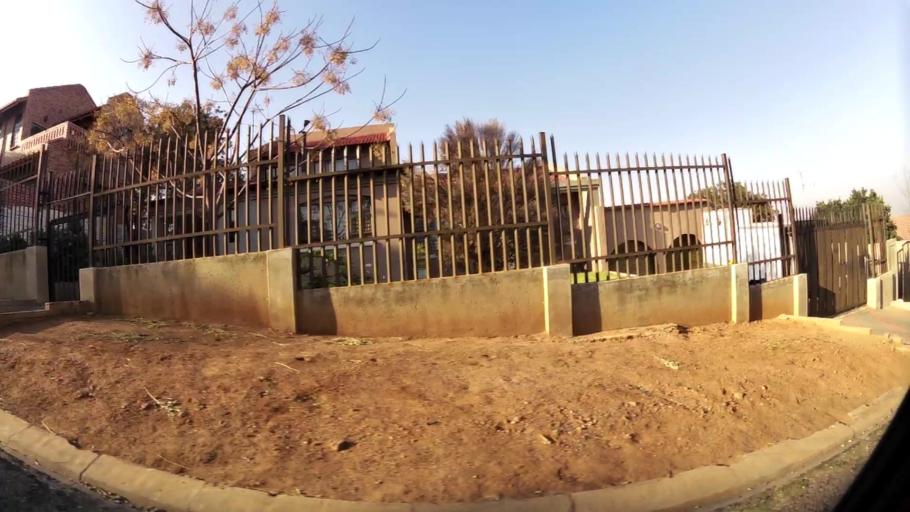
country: ZA
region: Gauteng
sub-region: City of Johannesburg Metropolitan Municipality
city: Soweto
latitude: -26.2919
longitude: 27.9558
